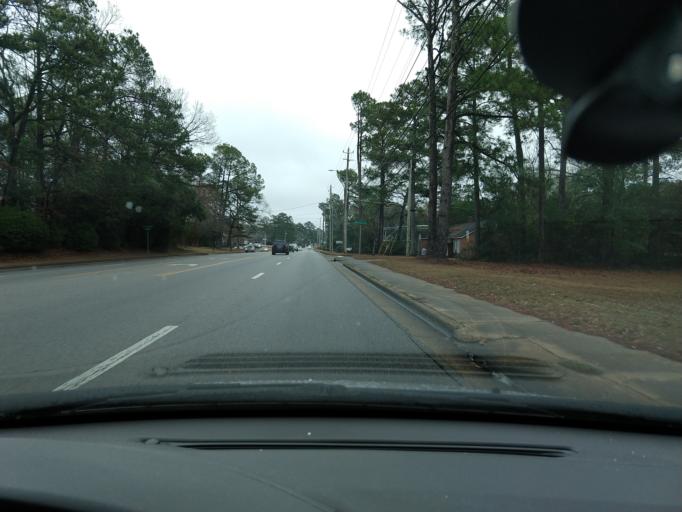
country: US
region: Alabama
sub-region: Houston County
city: Dothan
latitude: 31.2282
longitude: -85.4218
